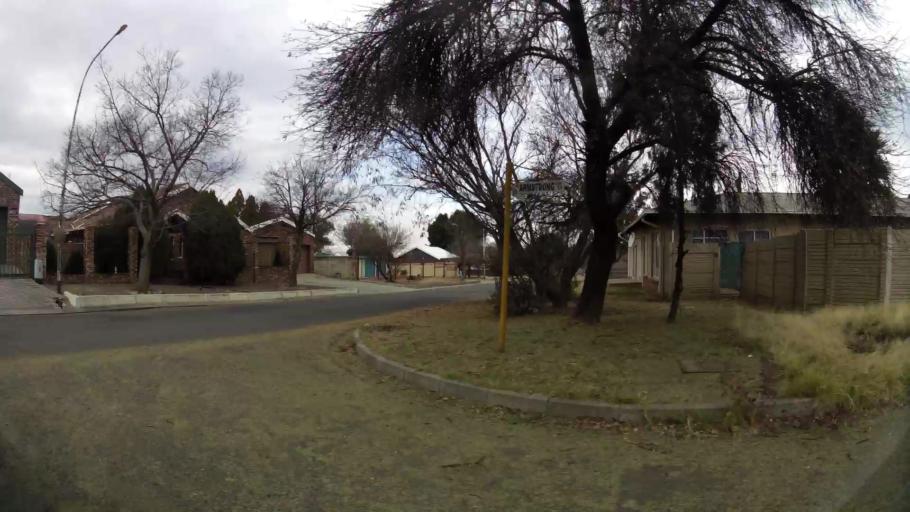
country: ZA
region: Orange Free State
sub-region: Fezile Dabi District Municipality
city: Kroonstad
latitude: -27.6500
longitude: 27.2464
